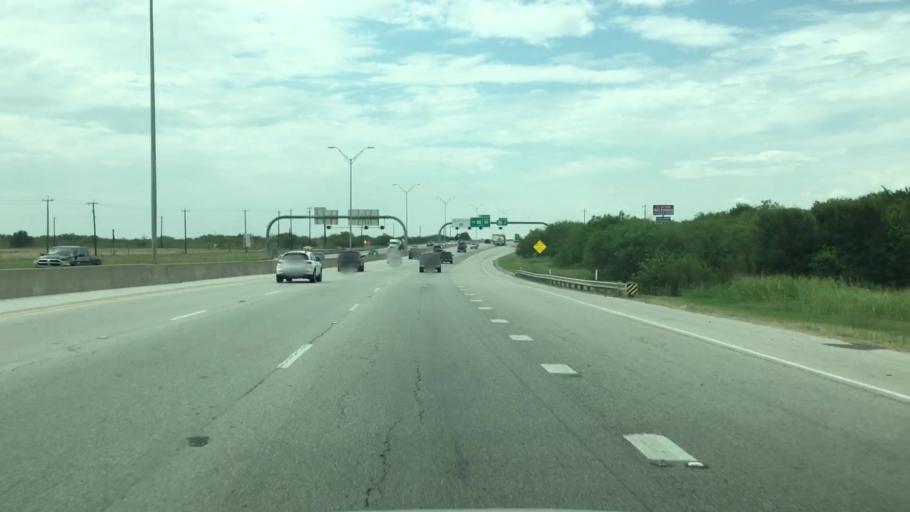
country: US
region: Texas
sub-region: Bexar County
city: Elmendorf
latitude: 29.3116
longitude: -98.4033
